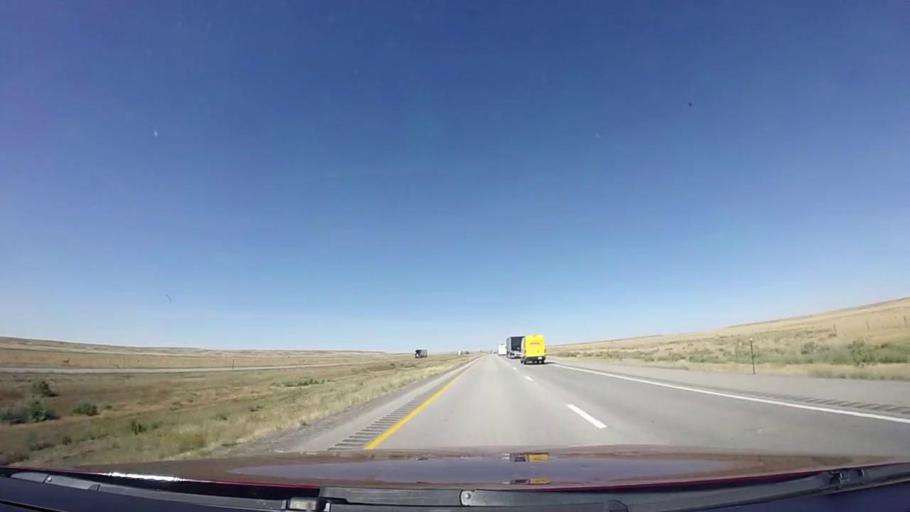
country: US
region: Wyoming
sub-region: Carbon County
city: Rawlins
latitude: 41.6624
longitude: -108.0535
